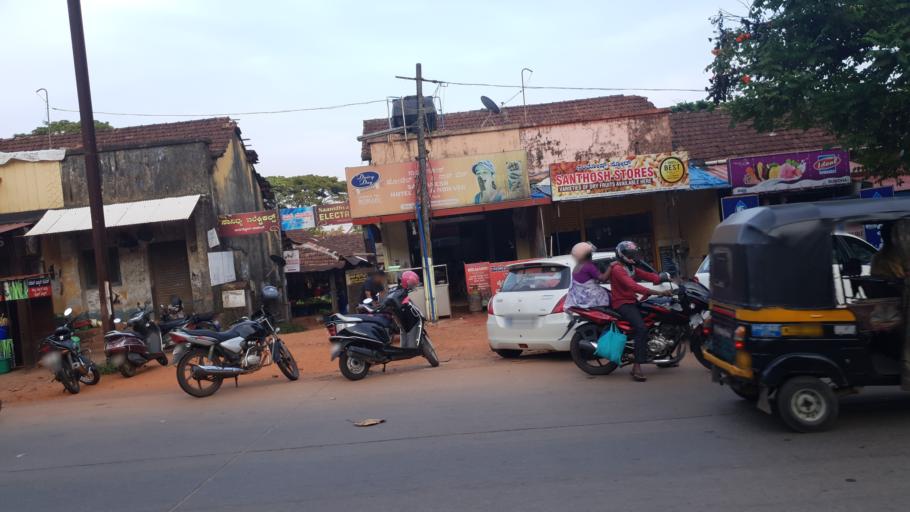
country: IN
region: Karnataka
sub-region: Dakshina Kannada
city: Mangalore
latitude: 12.9003
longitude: 74.8357
